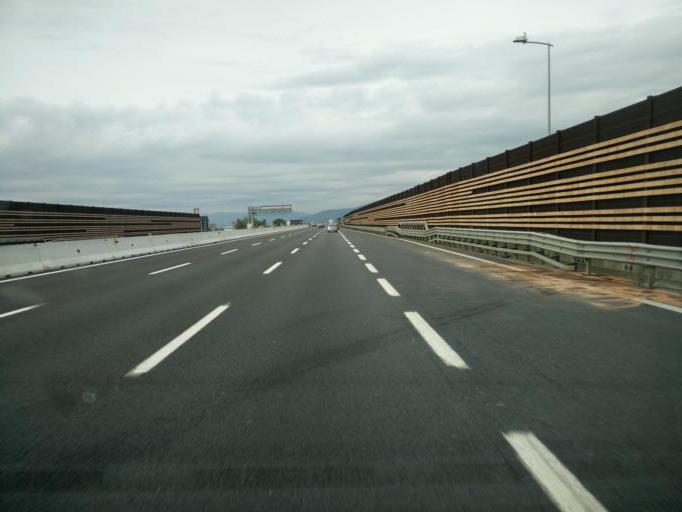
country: IT
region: Tuscany
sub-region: Province of Florence
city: Mantignano-Ugnano
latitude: 43.7807
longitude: 11.1606
